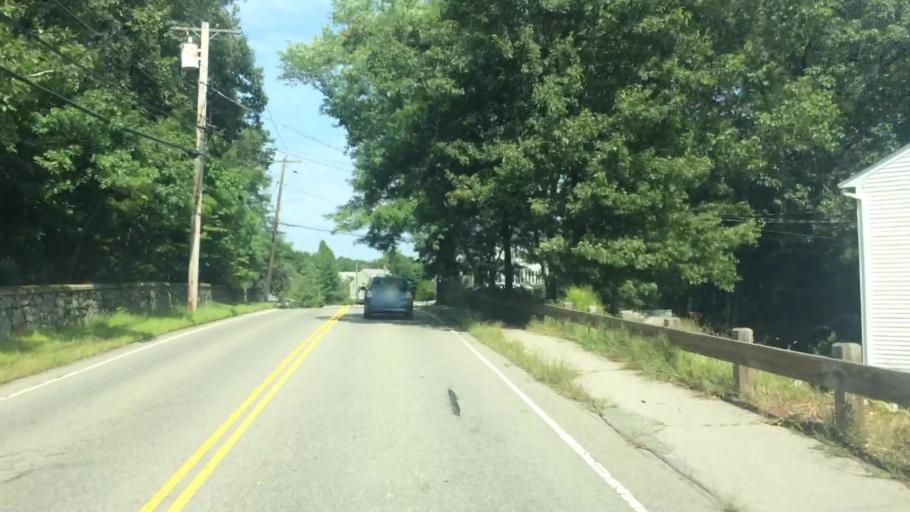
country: US
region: Massachusetts
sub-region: Norfolk County
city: Dedham
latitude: 42.2614
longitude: -71.1816
